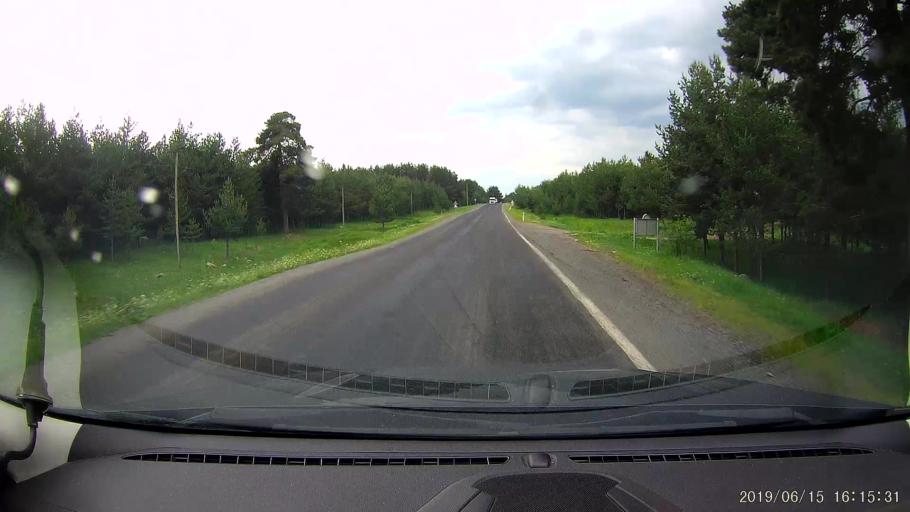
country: TR
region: Ardahan
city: Hanak
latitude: 41.2674
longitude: 42.8564
